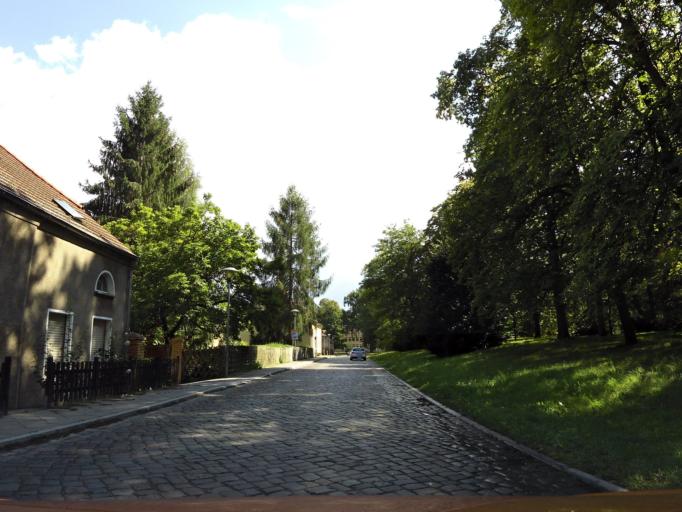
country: DE
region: Brandenburg
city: Ketzin
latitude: 52.4709
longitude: 12.8767
